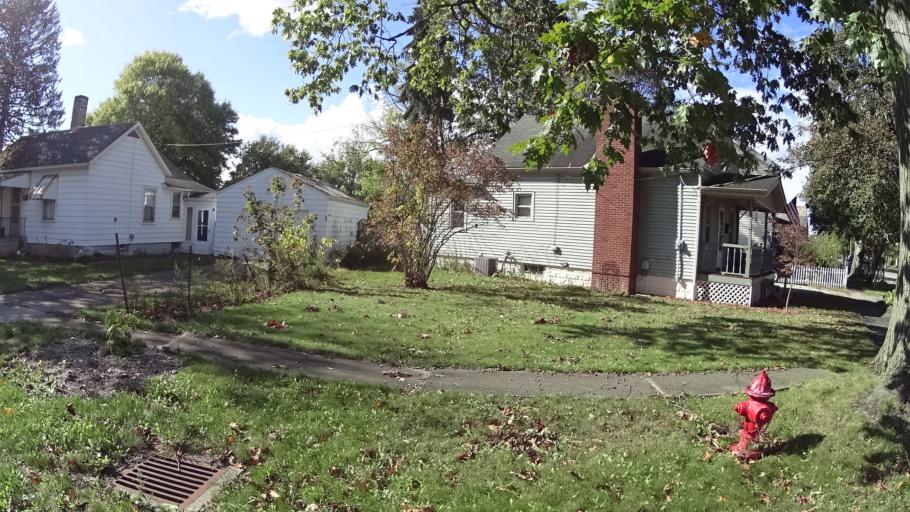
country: US
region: Ohio
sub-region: Lorain County
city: Grafton
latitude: 41.2766
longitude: -82.0582
